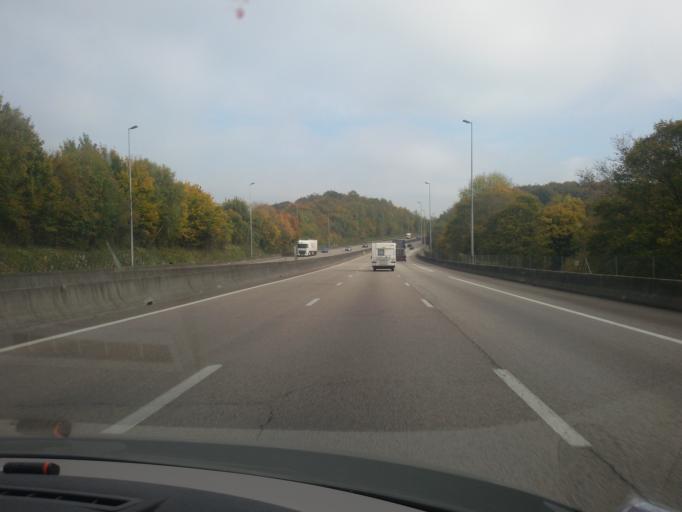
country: FR
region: Haute-Normandie
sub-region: Departement de la Seine-Maritime
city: Sahurs
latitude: 49.3390
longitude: 0.9589
